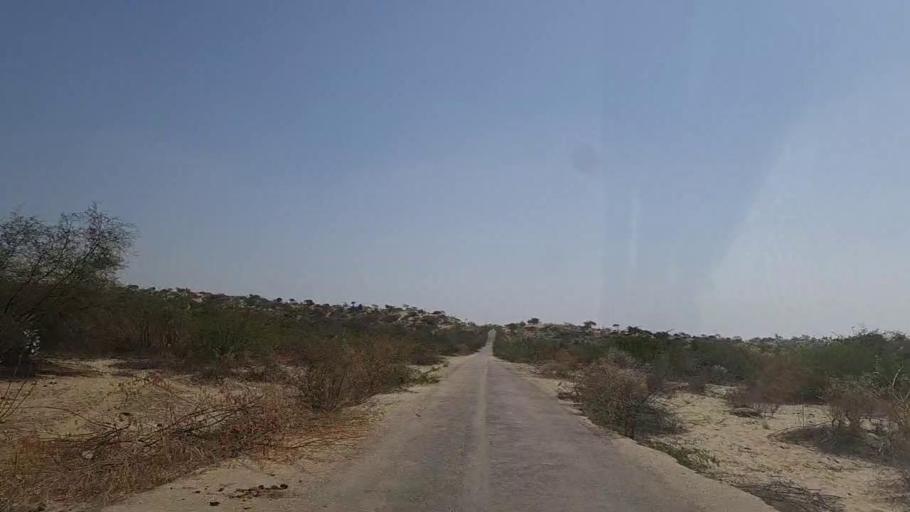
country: PK
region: Sindh
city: Diplo
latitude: 24.4926
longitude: 69.4357
